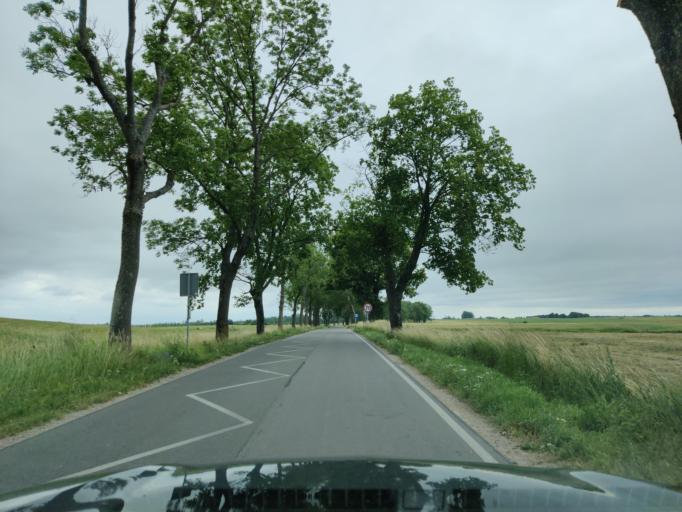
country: PL
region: Warmian-Masurian Voivodeship
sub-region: Powiat mragowski
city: Mikolajki
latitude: 53.8733
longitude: 21.5953
